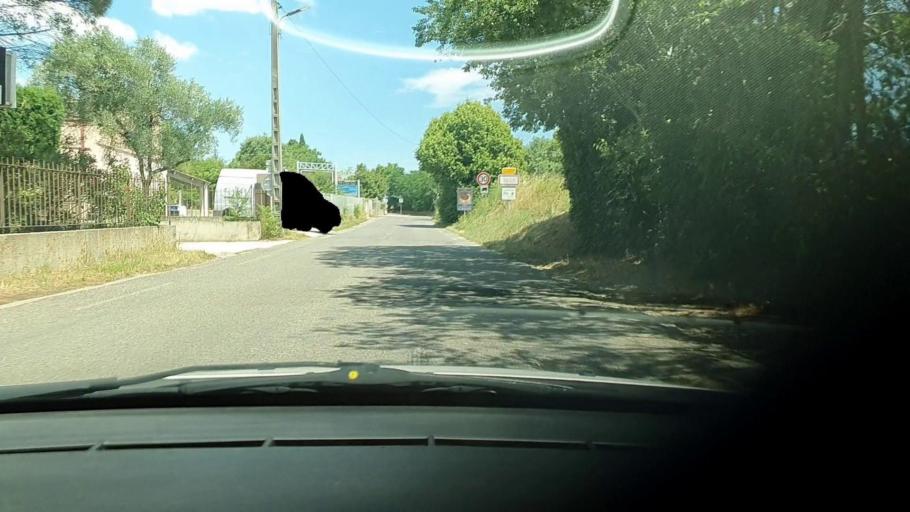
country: FR
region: Languedoc-Roussillon
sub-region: Departement du Gard
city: Uzes
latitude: 44.0178
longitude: 4.3996
